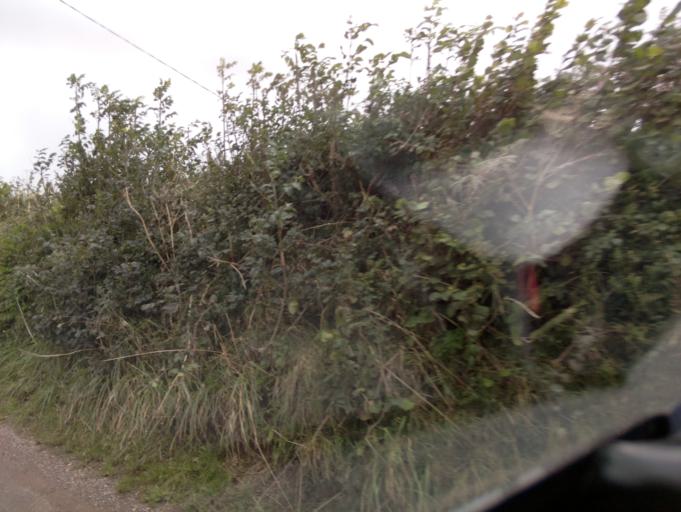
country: GB
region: England
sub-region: Devon
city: Dartmouth
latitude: 50.3410
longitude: -3.6350
